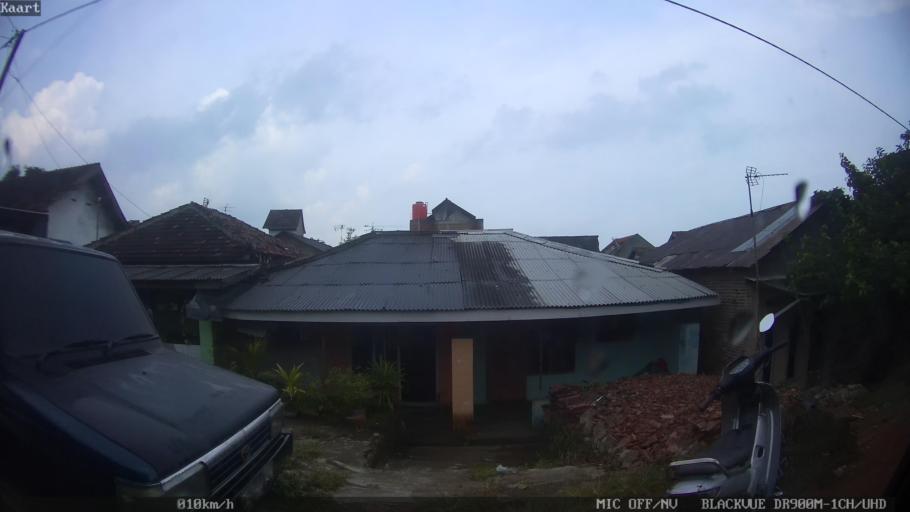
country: ID
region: Lampung
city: Bandarlampung
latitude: -5.4403
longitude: 105.2750
